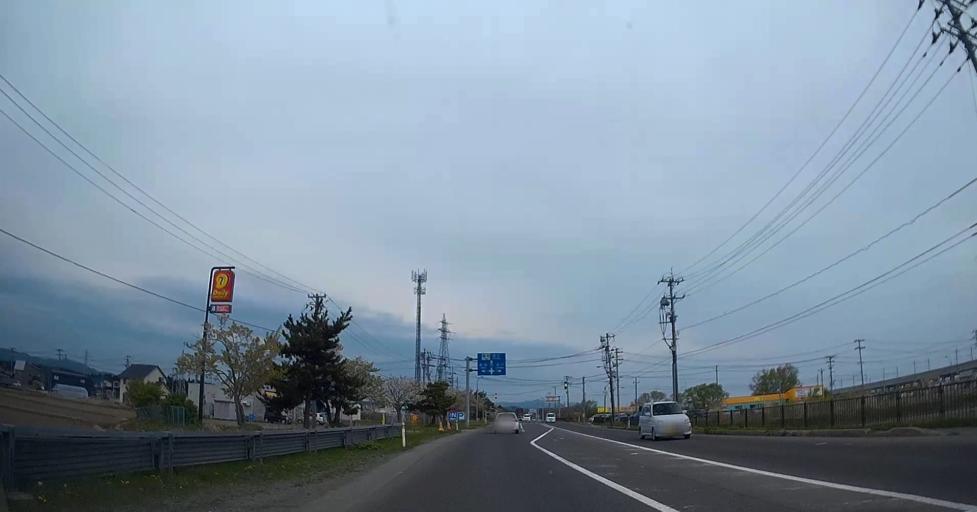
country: JP
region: Aomori
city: Aomori Shi
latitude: 40.8427
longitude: 140.6883
